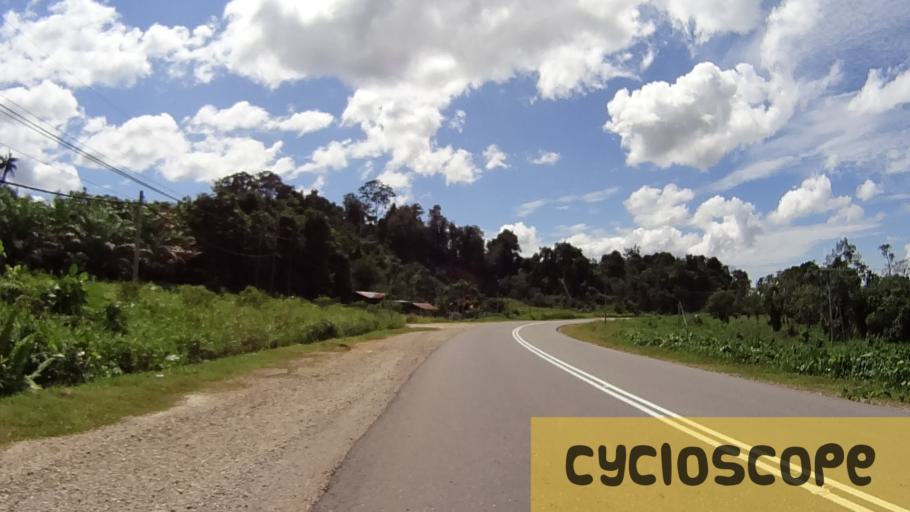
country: MY
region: Sabah
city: Beaufort
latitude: 5.2206
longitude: 115.6438
